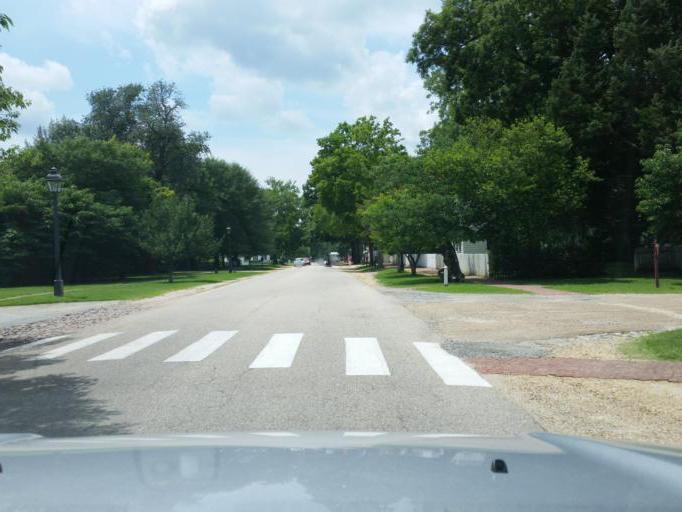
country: US
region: Virginia
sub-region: City of Williamsburg
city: Williamsburg
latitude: 37.2706
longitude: -76.6935
